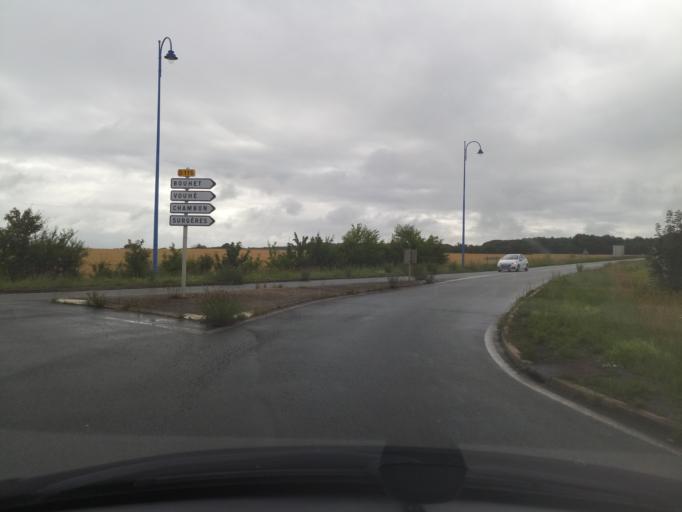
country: FR
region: Poitou-Charentes
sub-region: Departement de la Charente-Maritime
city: Courcon
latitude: 46.1825
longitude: -0.8557
